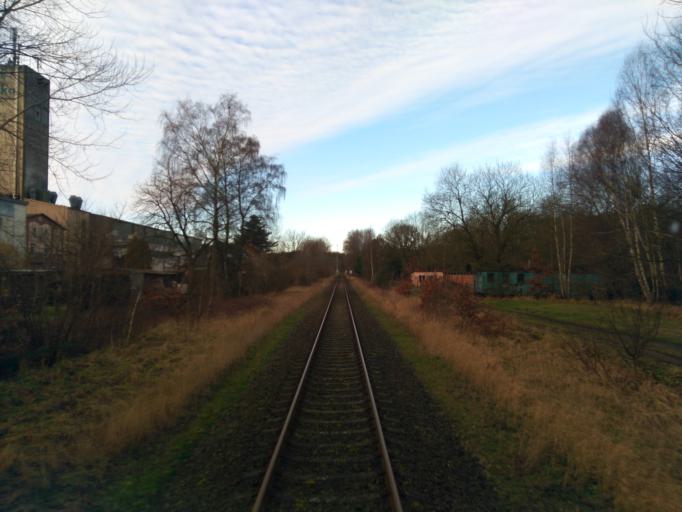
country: DE
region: Lower Saxony
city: Barum
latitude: 52.9971
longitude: 10.5042
